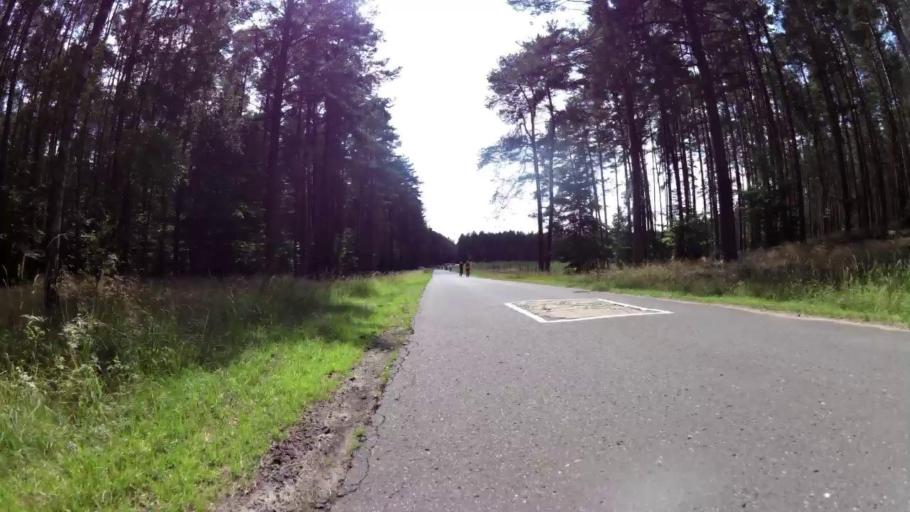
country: PL
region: West Pomeranian Voivodeship
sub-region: Powiat choszczenski
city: Drawno
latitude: 53.3680
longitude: 15.7200
